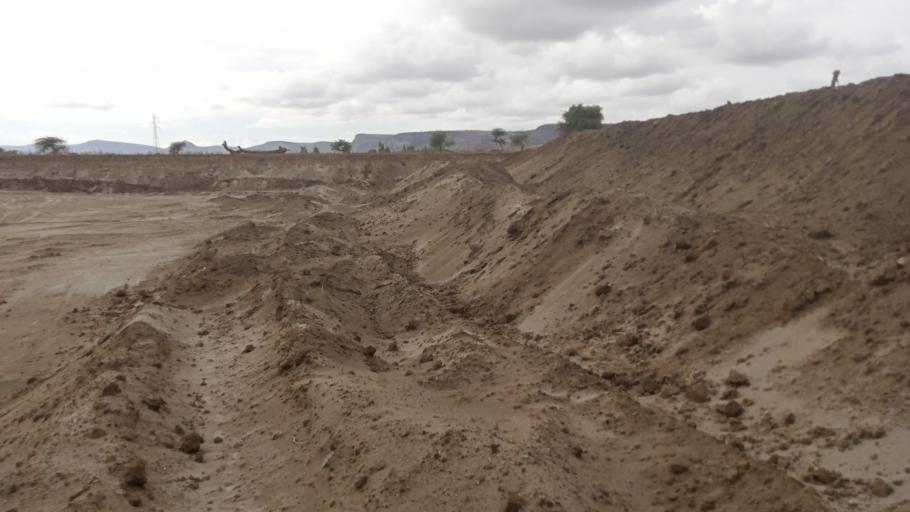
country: ET
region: Oromiya
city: Ziway
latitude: 7.9222
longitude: 38.6806
